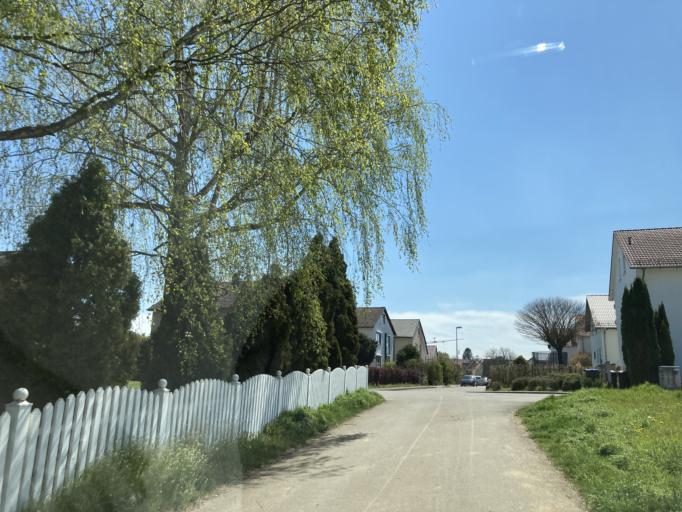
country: DE
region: Baden-Wuerttemberg
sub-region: Tuebingen Region
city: Rottenburg
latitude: 48.4855
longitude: 8.8856
